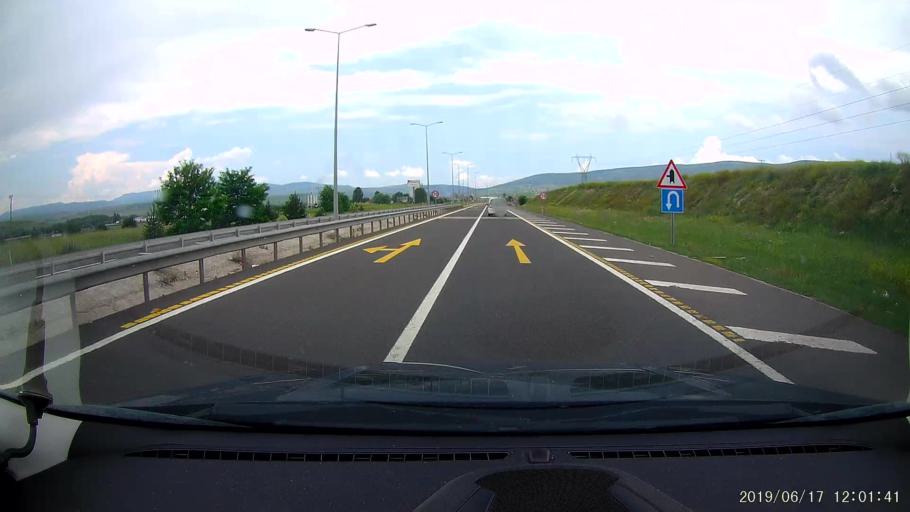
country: TR
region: Cankiri
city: Cerkes
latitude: 40.8222
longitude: 32.8620
